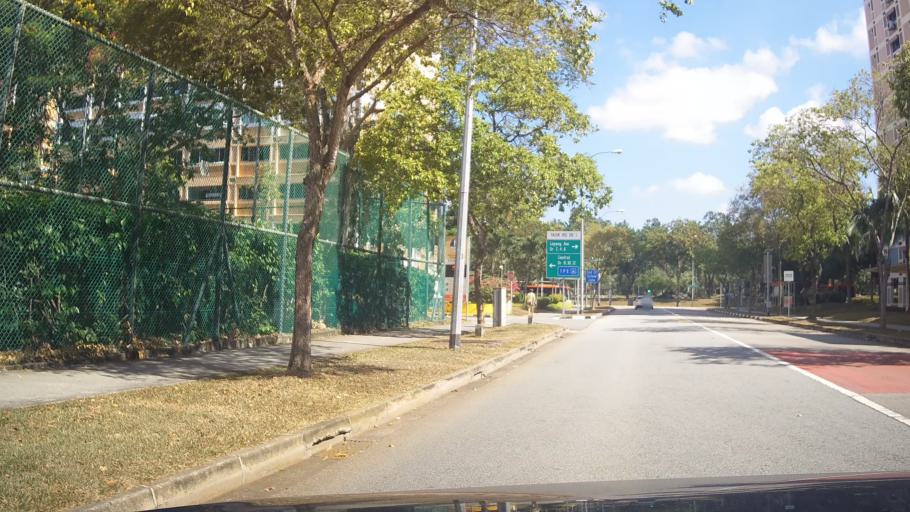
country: MY
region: Johor
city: Kampung Pasir Gudang Baru
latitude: 1.3685
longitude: 103.9517
